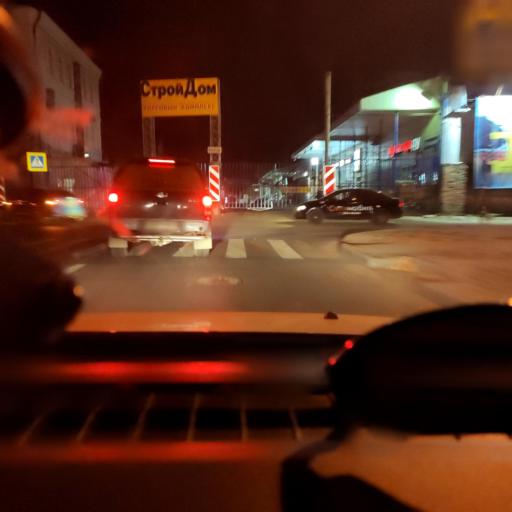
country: RU
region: Samara
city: Rozhdestveno
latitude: 53.1808
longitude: 50.0750
